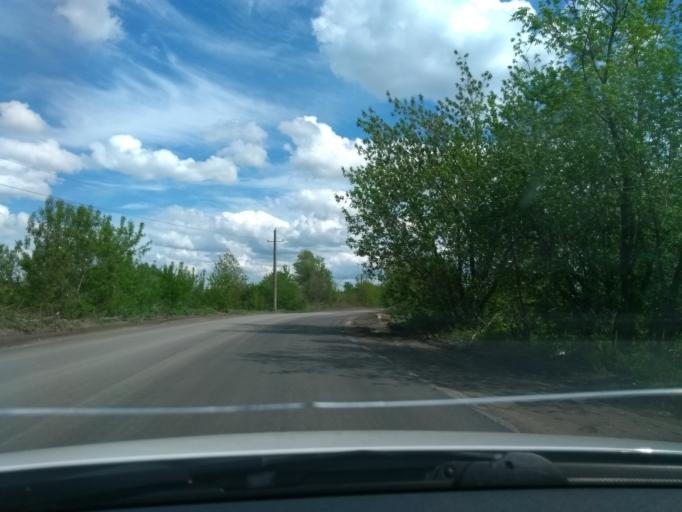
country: RU
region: Perm
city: Kondratovo
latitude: 58.0098
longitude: 56.0789
